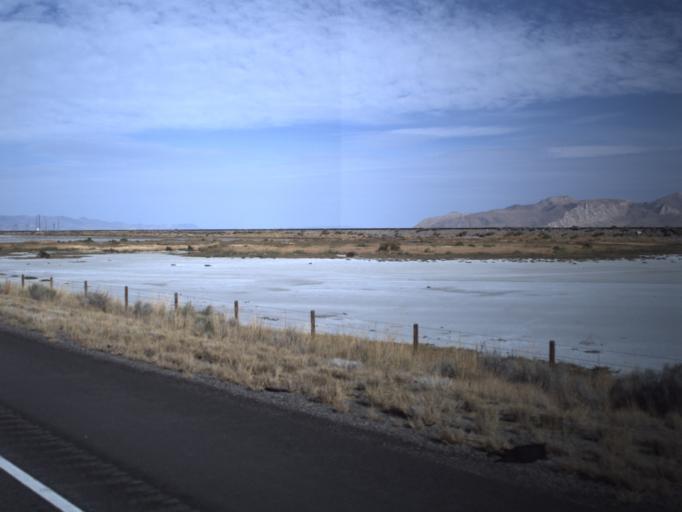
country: US
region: Utah
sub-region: Tooele County
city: Grantsville
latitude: 40.6820
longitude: -112.4273
